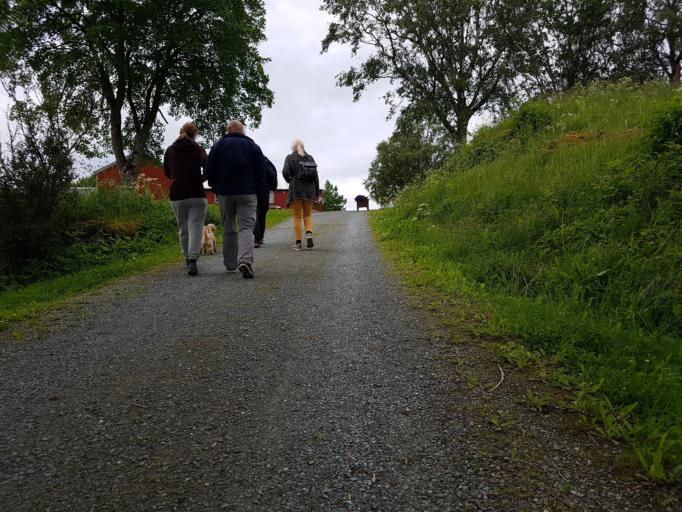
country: NO
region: Nord-Trondelag
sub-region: Frosta
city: Frosta
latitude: 63.5682
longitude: 10.7050
